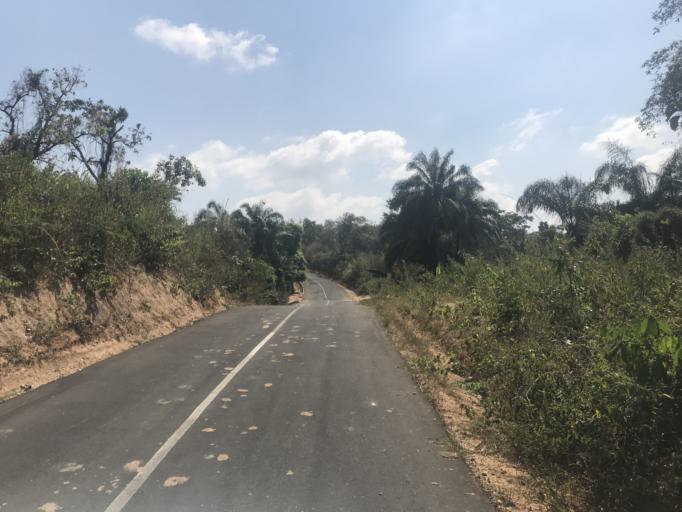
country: NG
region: Osun
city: Otan Ayegbaju
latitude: 7.8989
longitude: 4.8328
